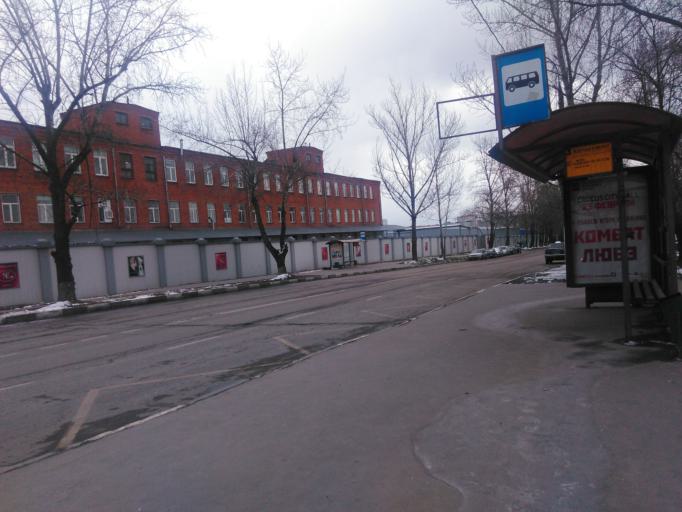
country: RU
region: Moscow
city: Nagornyy
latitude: 55.6470
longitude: 37.6327
